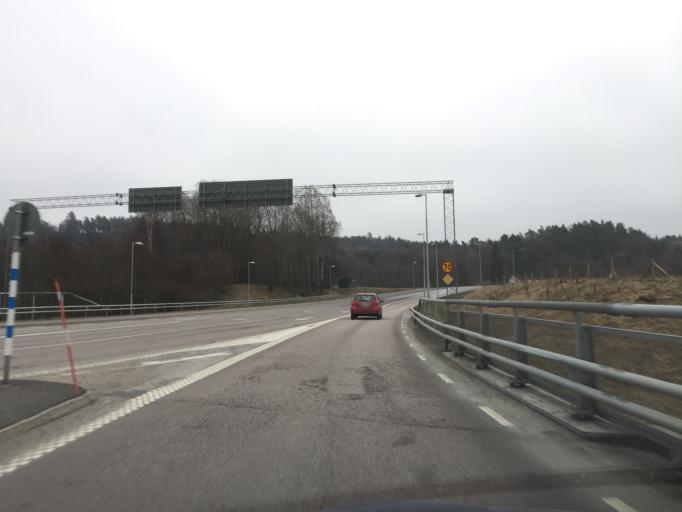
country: SE
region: Vaestra Goetaland
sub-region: Goteborg
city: Rannebergen
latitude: 57.7779
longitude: 12.0721
